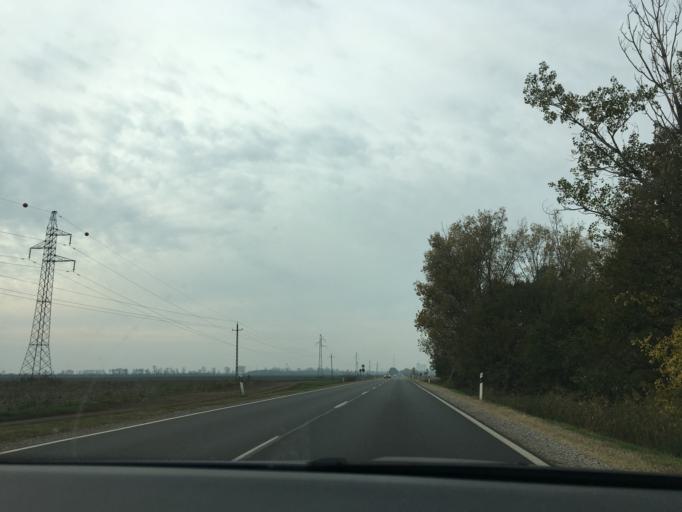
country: HU
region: Hajdu-Bihar
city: Puspokladany
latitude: 47.3404
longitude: 21.1720
